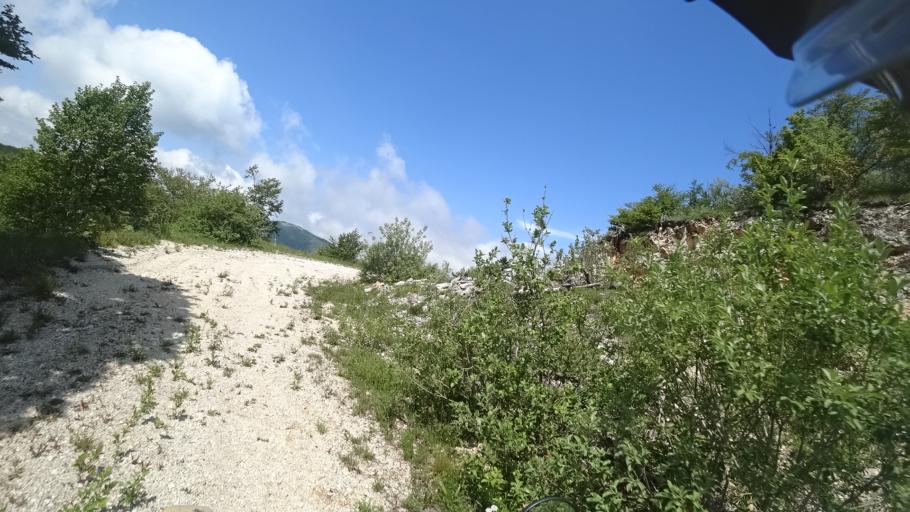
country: BA
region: Federation of Bosnia and Herzegovina
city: Orasac
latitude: 44.5661
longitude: 15.8566
